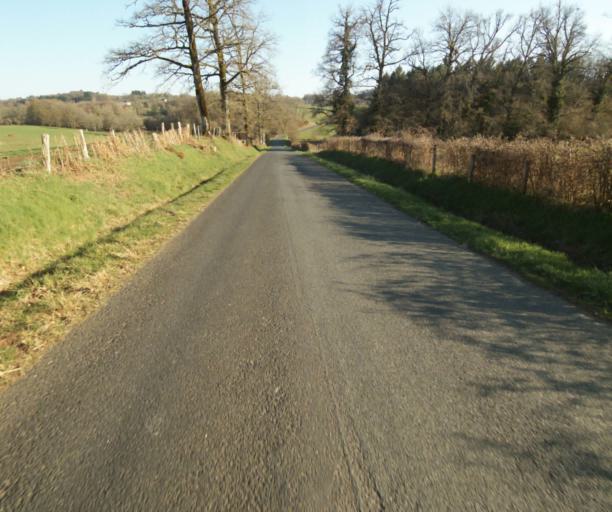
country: FR
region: Limousin
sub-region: Departement de la Correze
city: Saint-Clement
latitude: 45.3341
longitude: 1.6552
